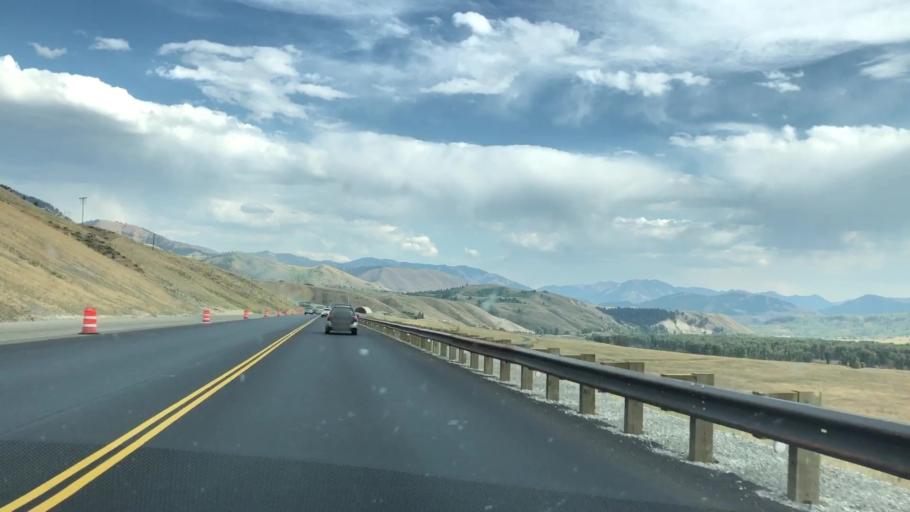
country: US
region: Wyoming
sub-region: Teton County
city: South Park
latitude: 43.4087
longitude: -110.7664
